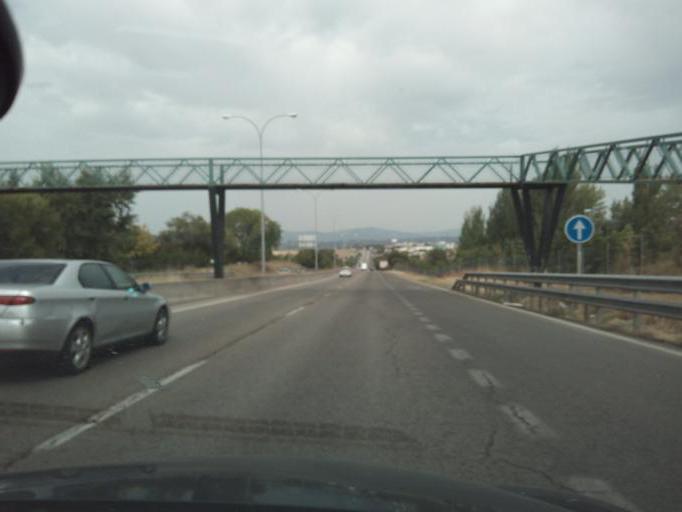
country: ES
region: Madrid
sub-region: Provincia de Madrid
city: Las Rozas de Madrid
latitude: 40.4921
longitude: -3.8794
